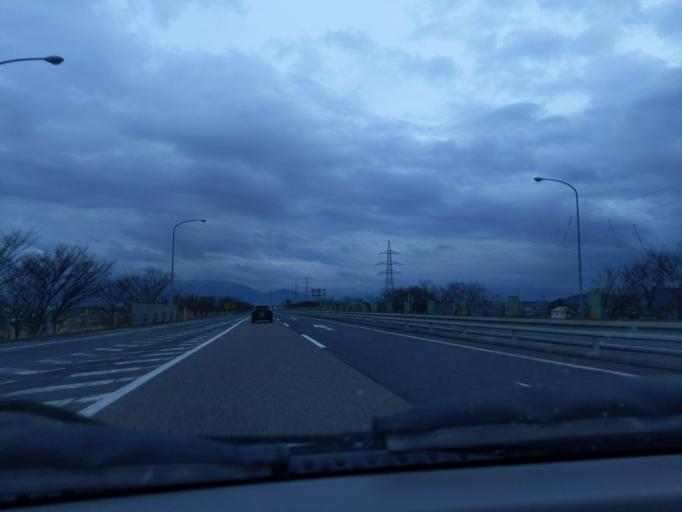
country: JP
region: Niigata
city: Niitsu-honcho
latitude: 37.8036
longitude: 139.1515
